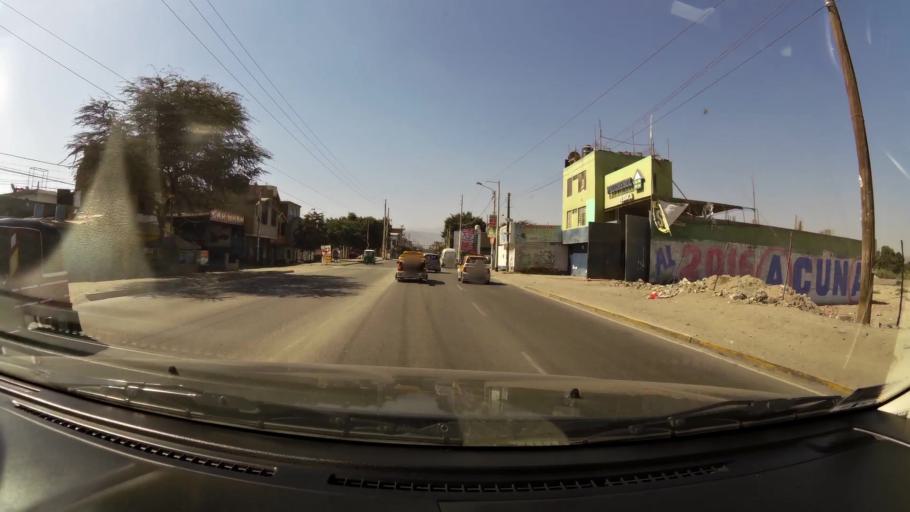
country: PE
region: Ica
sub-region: Provincia de Ica
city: La Tinguina
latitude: -14.0527
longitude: -75.7051
